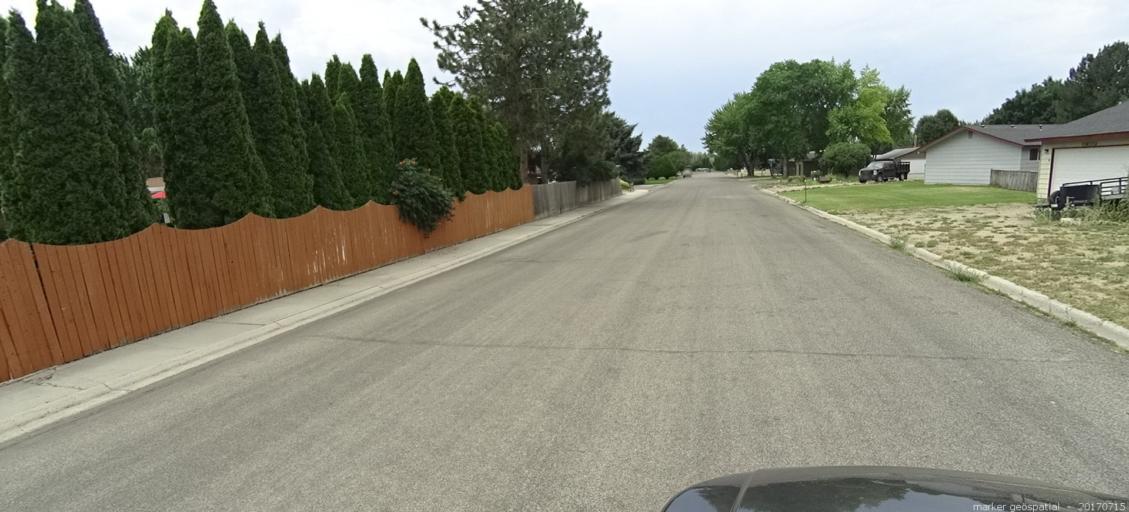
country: US
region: Idaho
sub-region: Ada County
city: Garden City
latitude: 43.5538
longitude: -116.2998
